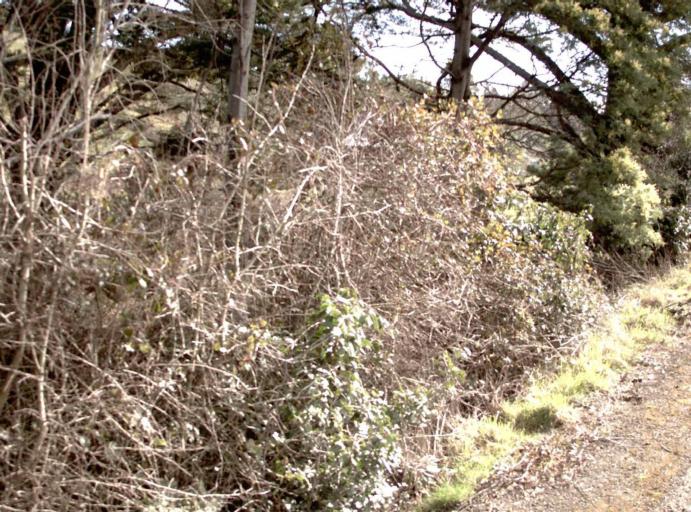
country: AU
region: Tasmania
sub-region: Launceston
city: Mayfield
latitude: -41.2470
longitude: 147.2464
